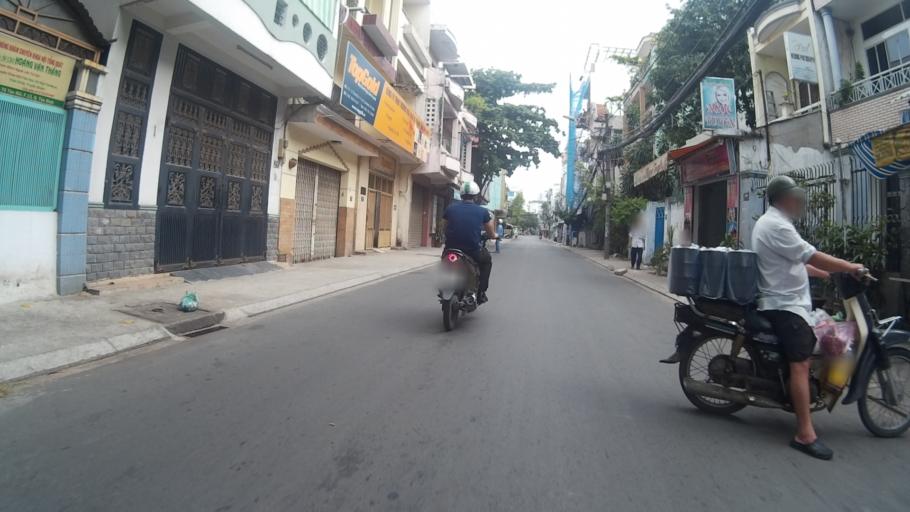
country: VN
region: Ho Chi Minh City
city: Quan Tan Phu
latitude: 10.8024
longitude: 106.6385
